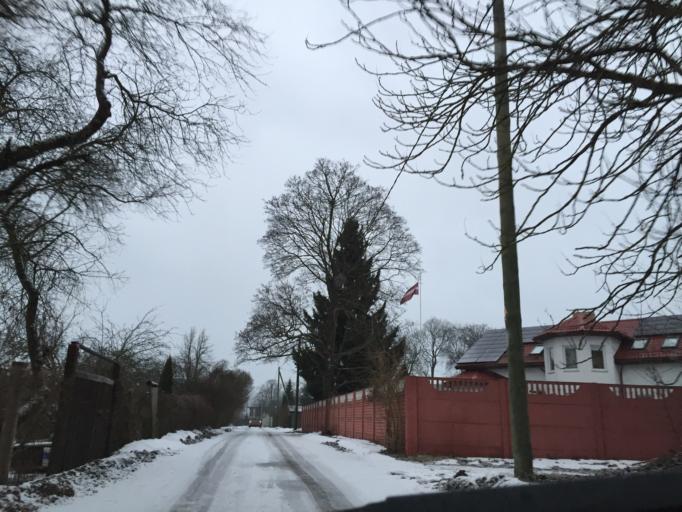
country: LV
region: Riga
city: Riga
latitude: 56.9221
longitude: 24.1287
